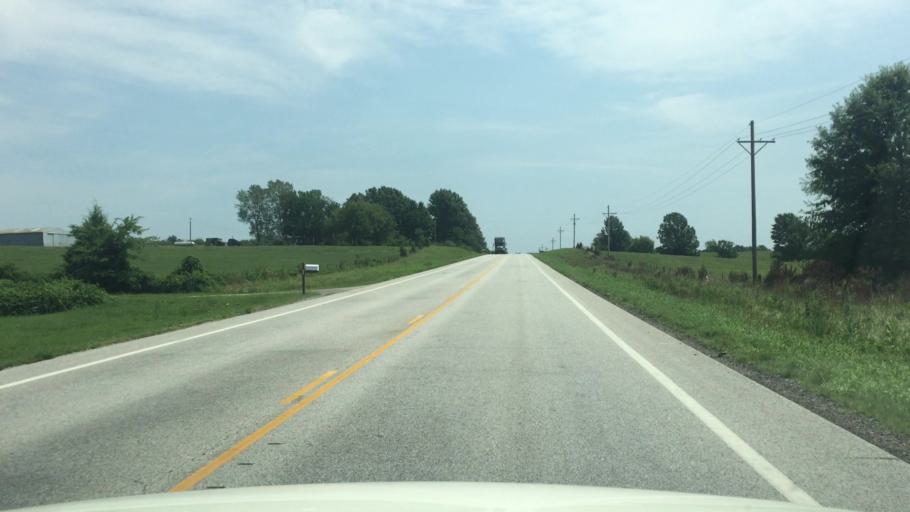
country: US
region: Kansas
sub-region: Cherokee County
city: Columbus
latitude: 37.1780
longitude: -94.7915
